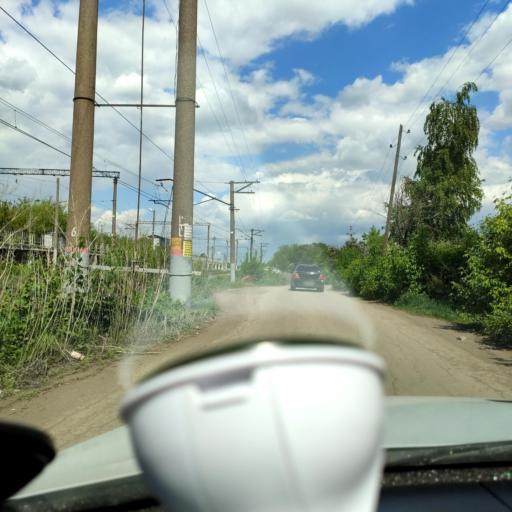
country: RU
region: Samara
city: Petra-Dubrava
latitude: 53.2702
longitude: 50.3175
